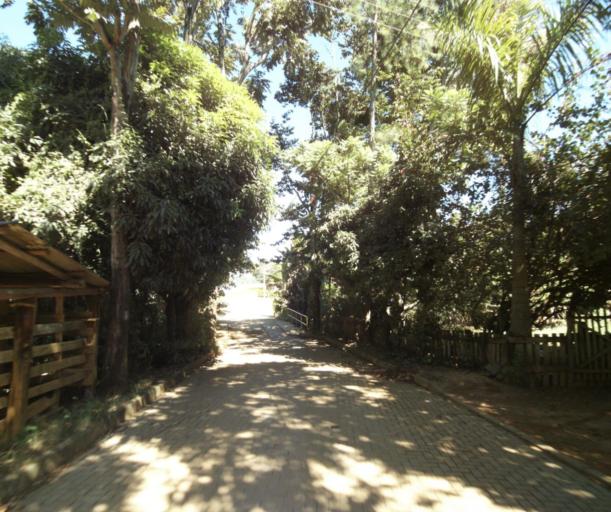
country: BR
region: Minas Gerais
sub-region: Espera Feliz
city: Espera Feliz
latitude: -20.5508
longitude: -41.8111
